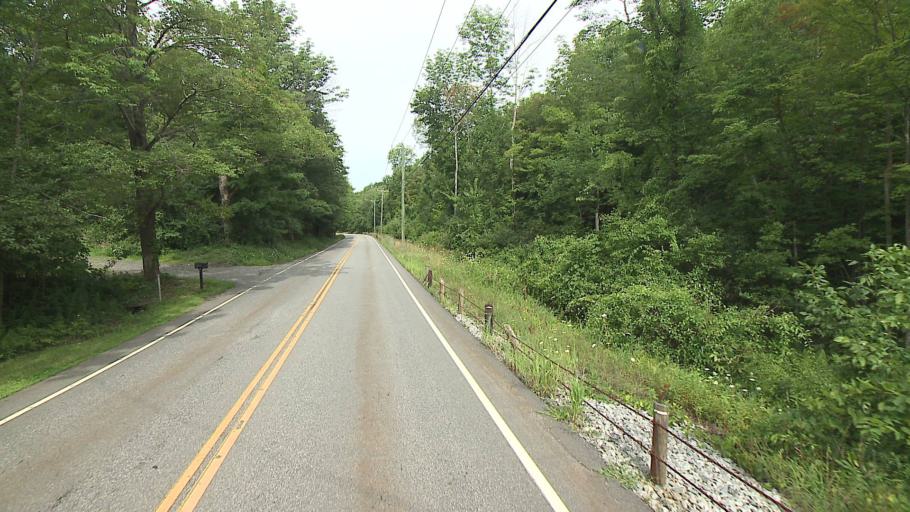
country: US
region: Connecticut
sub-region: Litchfield County
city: Kent
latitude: 41.7155
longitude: -73.4377
